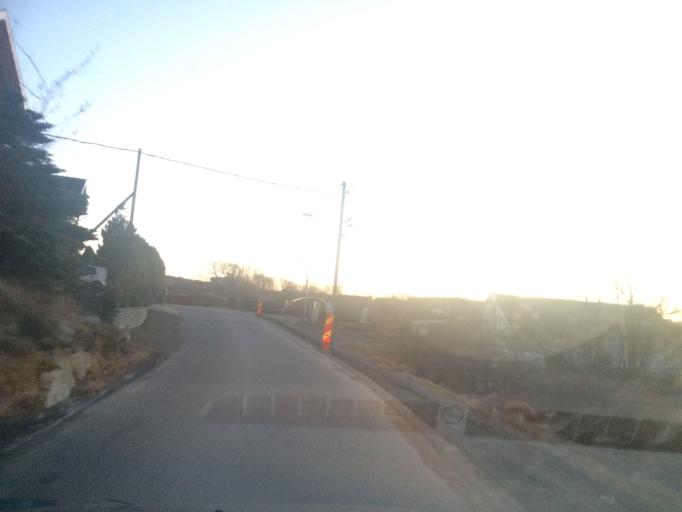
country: SE
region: Vaestra Goetaland
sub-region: Goteborg
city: Torslanda
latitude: 57.7787
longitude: 11.8278
